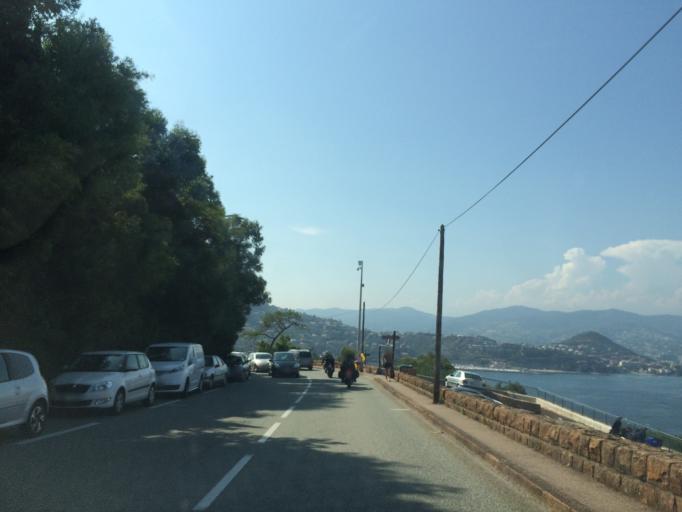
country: FR
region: Provence-Alpes-Cote d'Azur
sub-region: Departement des Alpes-Maritimes
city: Theoule-sur-Mer
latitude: 43.5048
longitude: 6.9528
